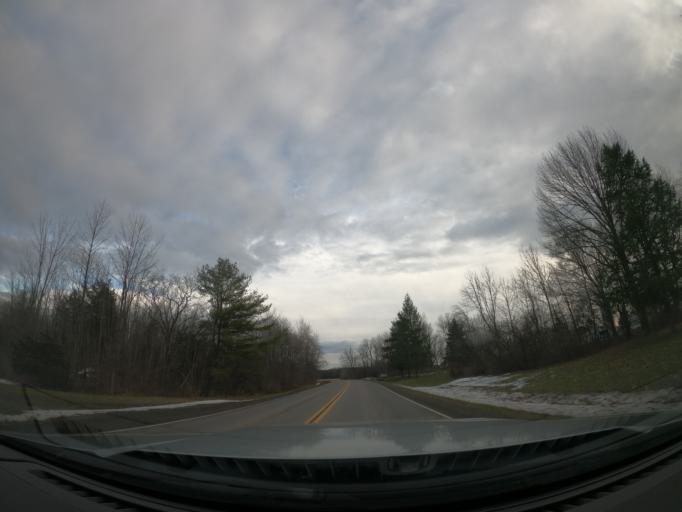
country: US
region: New York
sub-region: Yates County
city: Dundee
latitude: 42.5006
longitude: -76.9527
